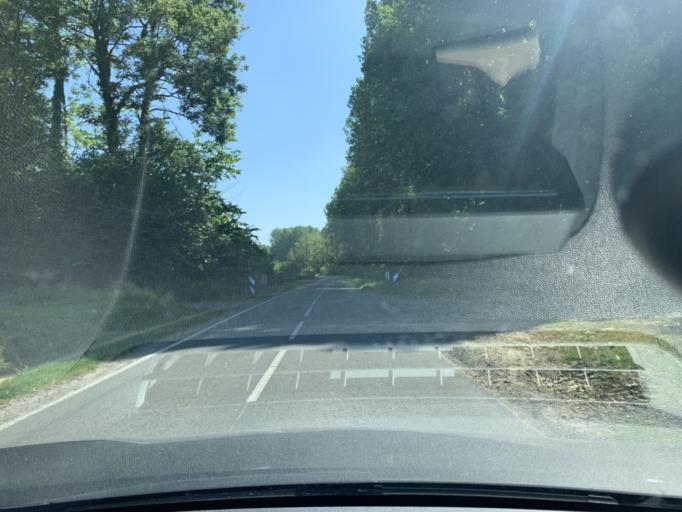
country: FR
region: Nord-Pas-de-Calais
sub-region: Departement du Nord
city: Fontaine-Notre-Dame
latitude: 50.1529
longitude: 3.1754
